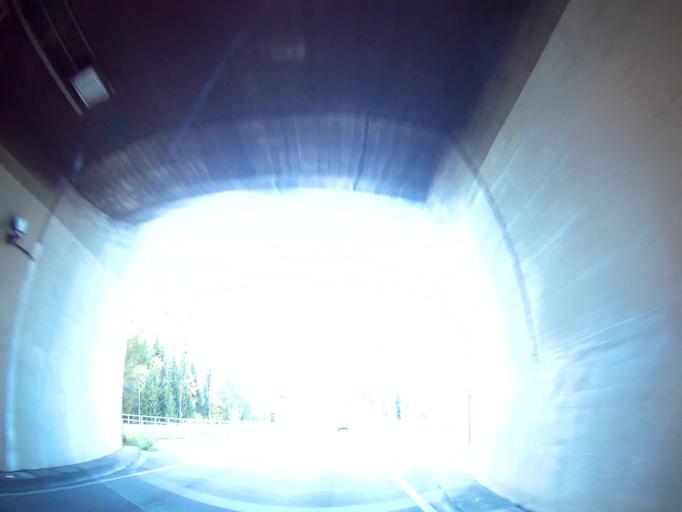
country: AT
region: Carinthia
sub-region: Politischer Bezirk Wolfsberg
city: Wolfsberg
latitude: 46.8993
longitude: 14.8212
